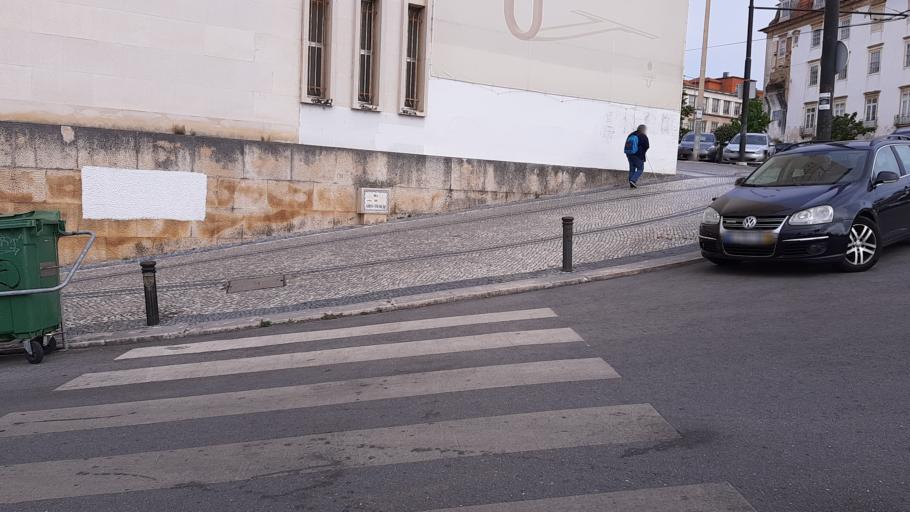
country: PT
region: Coimbra
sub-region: Coimbra
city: Coimbra
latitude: 40.2076
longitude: -8.4223
